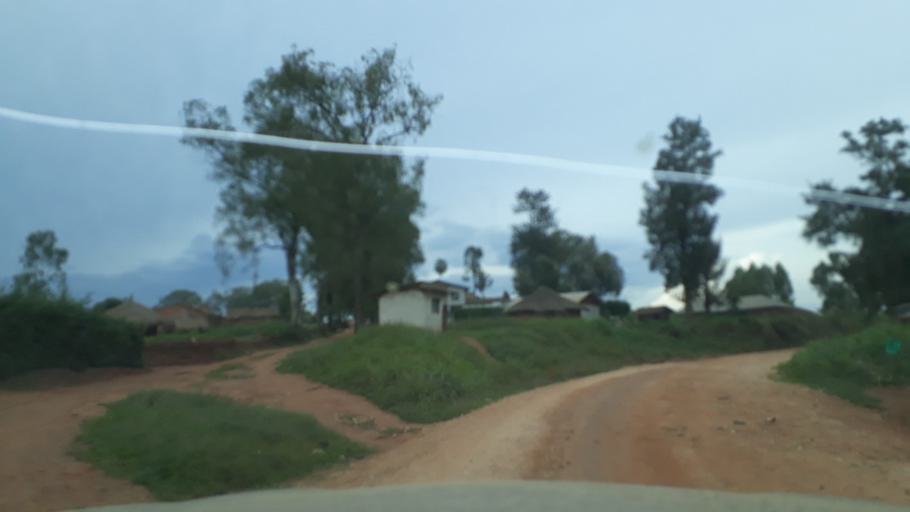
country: CD
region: Eastern Province
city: Bunia
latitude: 1.9140
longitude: 30.5026
